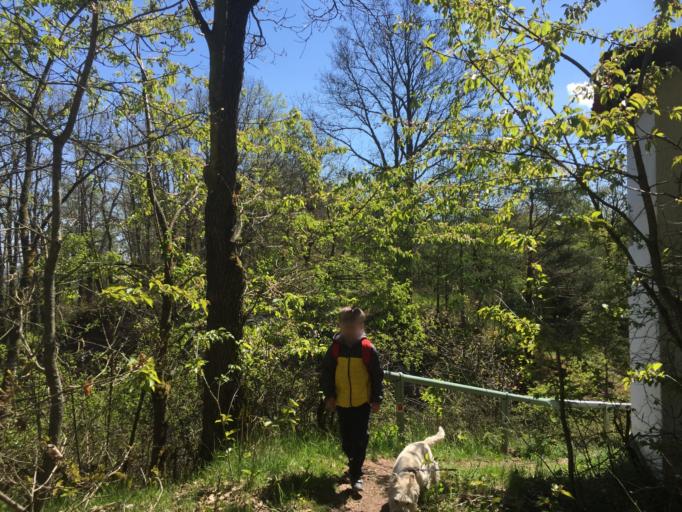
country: DE
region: Bavaria
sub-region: Regierungsbezirk Unterfranken
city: Sulzfeld
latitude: 50.2732
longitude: 10.4198
